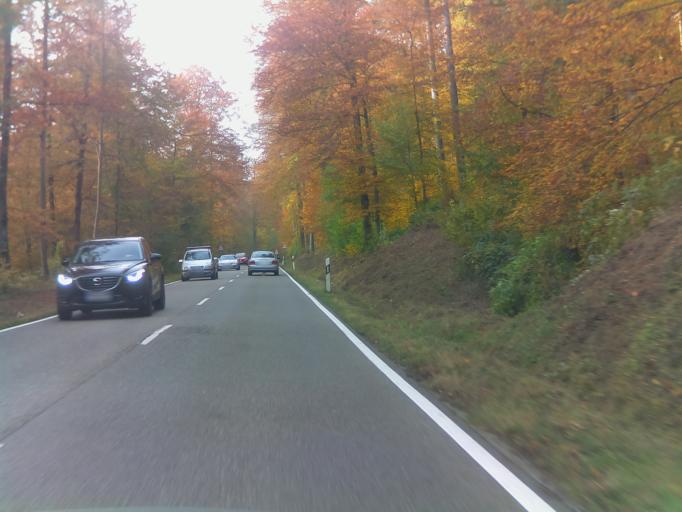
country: DE
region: Baden-Wuerttemberg
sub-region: Karlsruhe Region
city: Bammental
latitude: 49.3597
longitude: 8.7667
